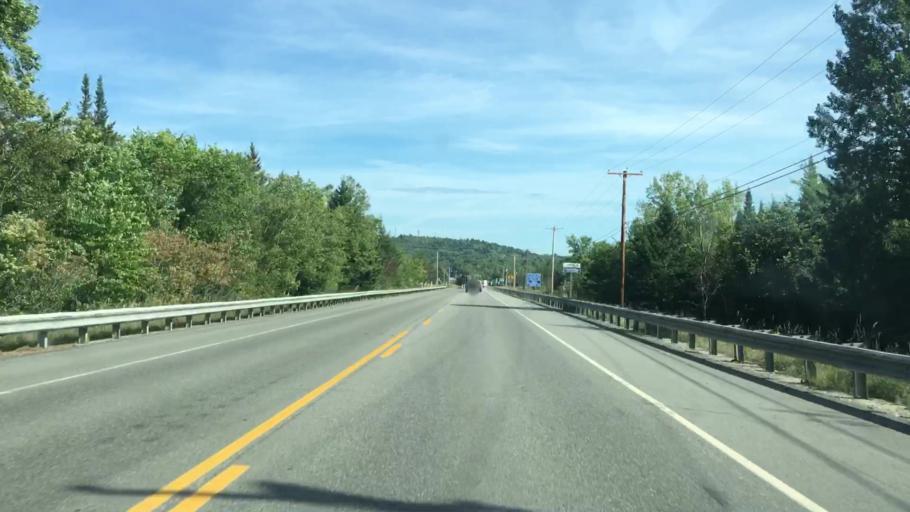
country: US
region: Maine
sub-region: Penobscot County
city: Lincoln
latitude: 45.3562
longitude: -68.5384
